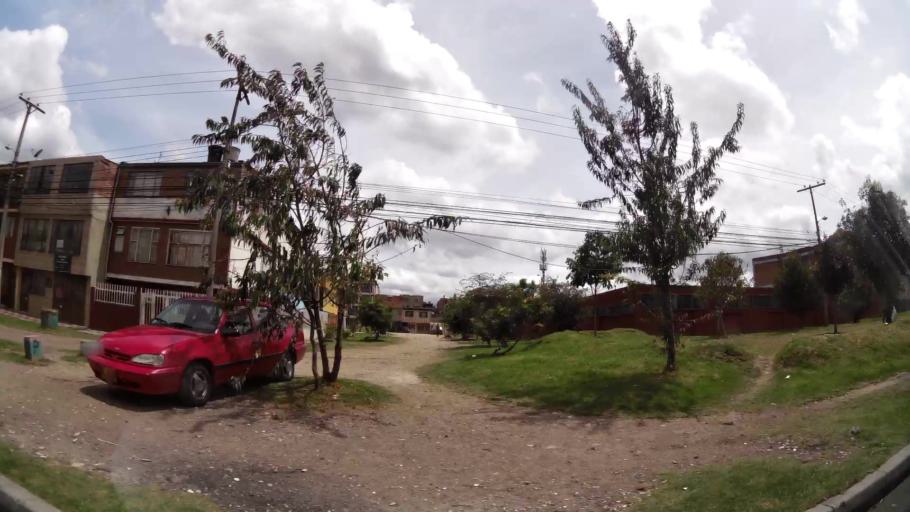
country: CO
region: Cundinamarca
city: Funza
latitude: 4.7083
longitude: -74.1200
